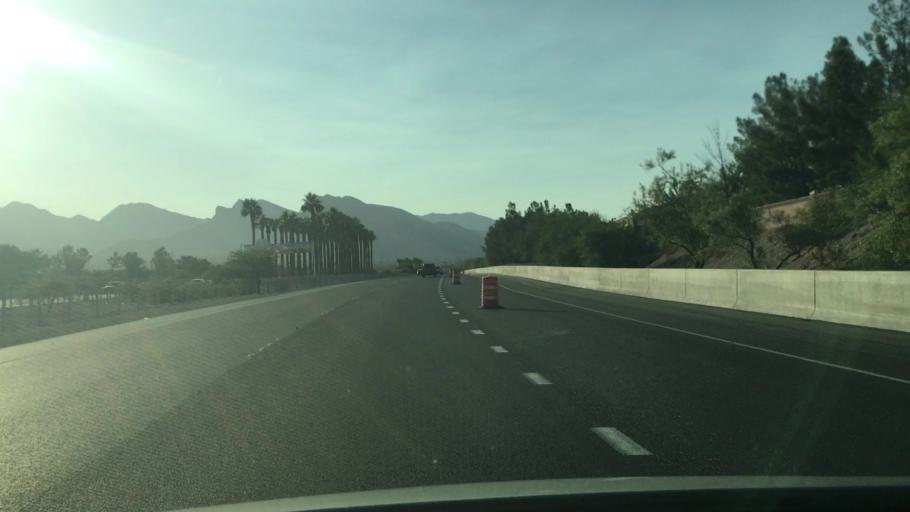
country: US
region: Nevada
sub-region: Clark County
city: Summerlin South
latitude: 36.1800
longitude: -115.2969
